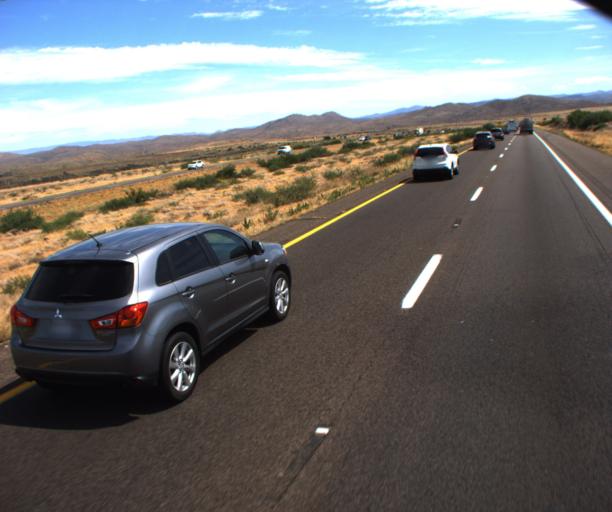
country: US
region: Arizona
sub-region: Yavapai County
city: Cordes Lakes
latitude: 34.2092
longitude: -112.1174
